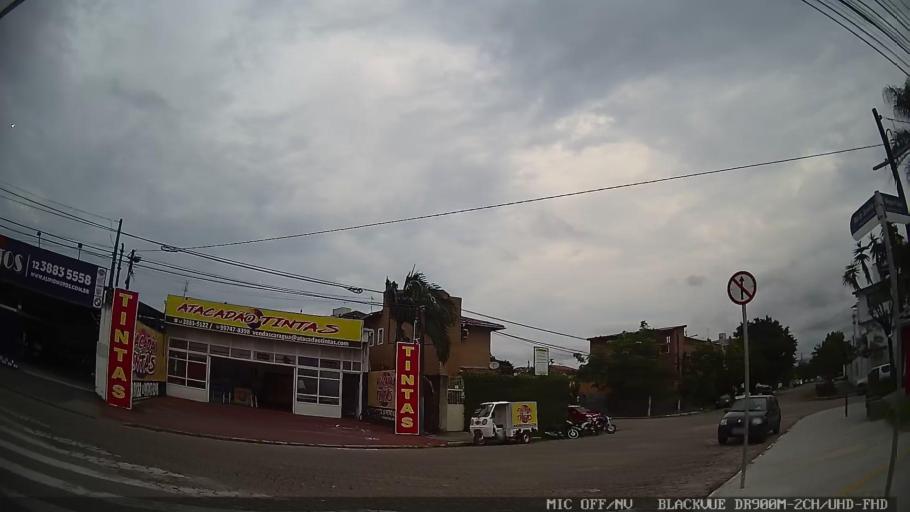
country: BR
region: Sao Paulo
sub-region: Caraguatatuba
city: Caraguatatuba
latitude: -23.6243
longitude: -45.4166
